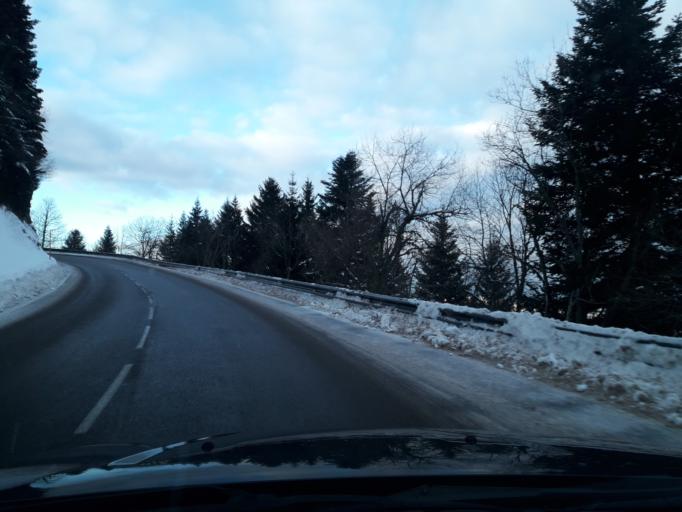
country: FR
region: Rhone-Alpes
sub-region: Departement de l'Isere
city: Revel
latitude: 45.1342
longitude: 5.8768
